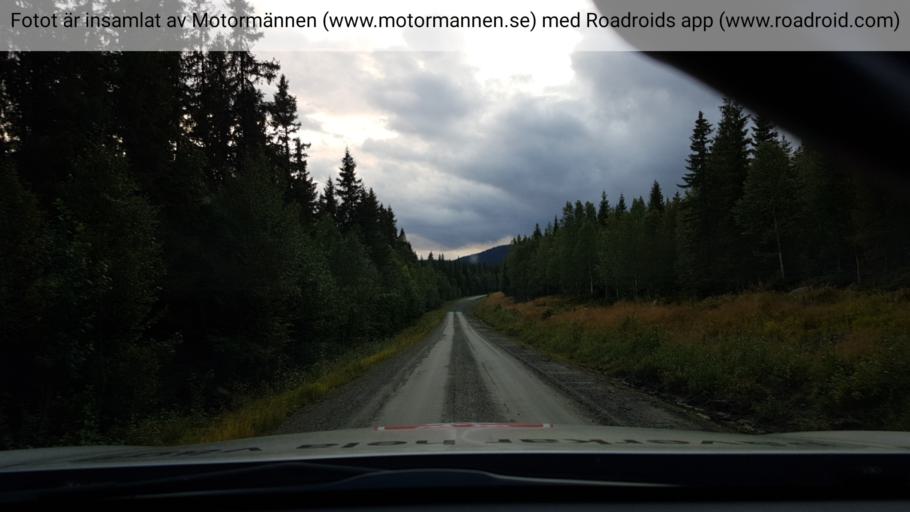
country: SE
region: Vaesterbotten
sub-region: Vilhelmina Kommun
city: Sjoberg
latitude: 65.4986
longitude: 15.6124
